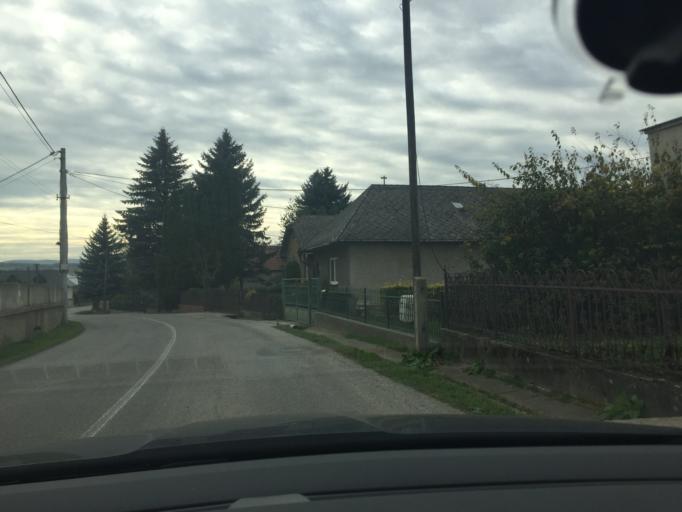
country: SK
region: Kosicky
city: Kosice
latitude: 48.8143
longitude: 21.3223
